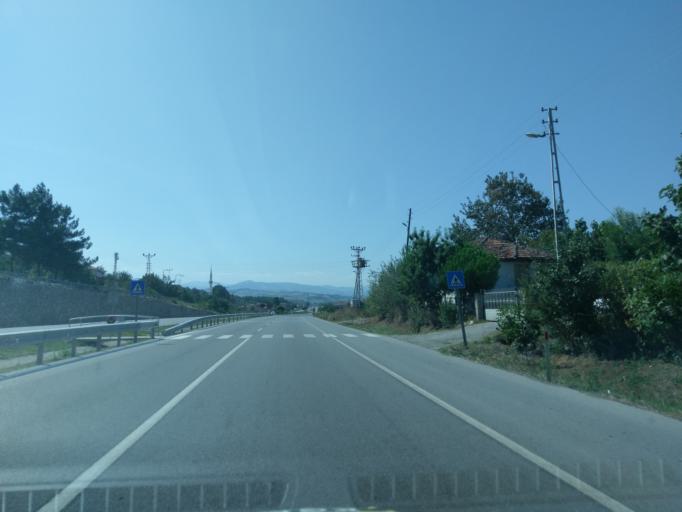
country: TR
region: Samsun
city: Alacam
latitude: 41.6084
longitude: 35.6880
